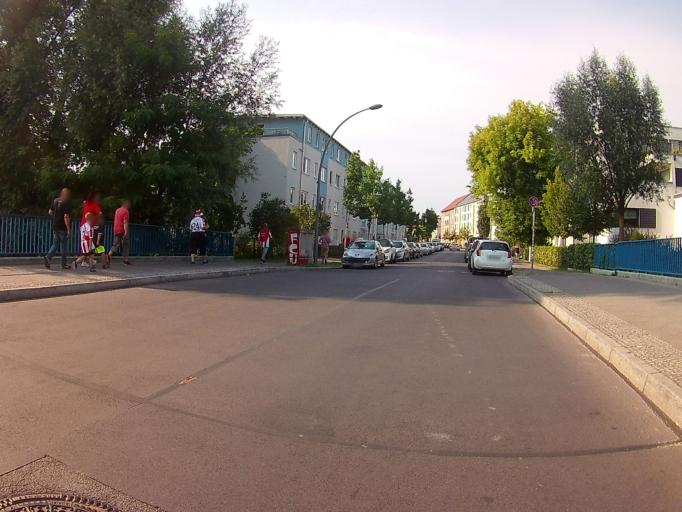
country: DE
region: Berlin
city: Kopenick Bezirk
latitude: 52.4569
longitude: 13.5741
